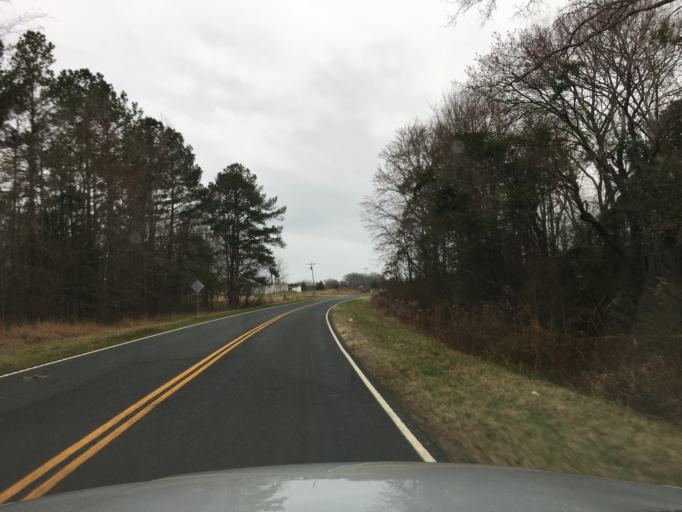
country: US
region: South Carolina
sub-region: Greenwood County
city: Greenwood
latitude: 34.1266
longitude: -82.1590
